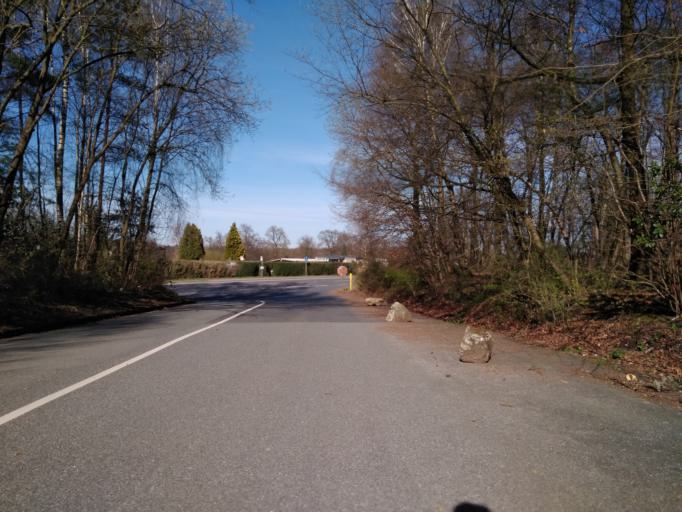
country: DE
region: North Rhine-Westphalia
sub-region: Regierungsbezirk Dusseldorf
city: Schermbeck
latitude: 51.6698
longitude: 6.8405
